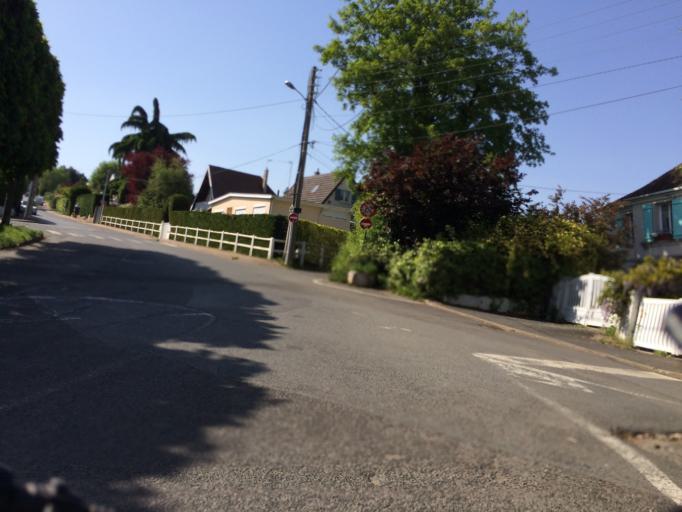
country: FR
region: Ile-de-France
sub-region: Departement de l'Essonne
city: Verrieres-le-Buisson
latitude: 48.7472
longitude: 2.2578
